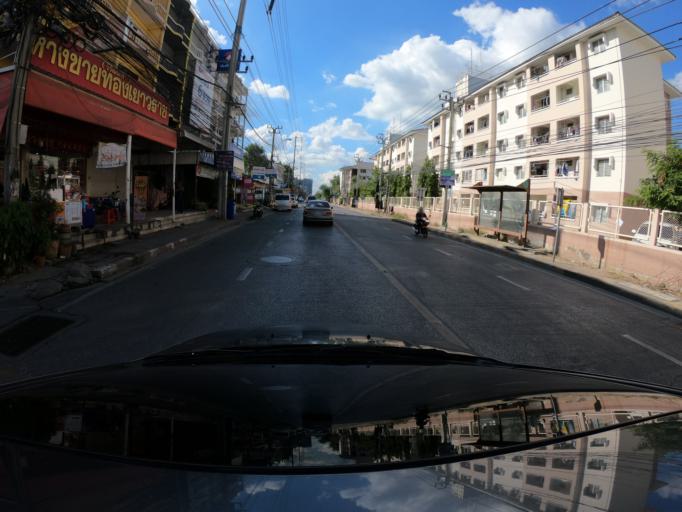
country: TH
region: Bangkok
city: Bang Na
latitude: 13.6530
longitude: 100.6155
